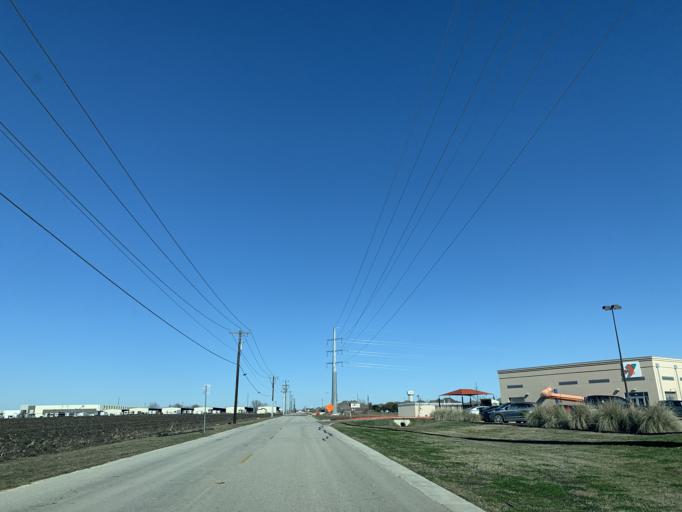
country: US
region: Texas
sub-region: Williamson County
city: Hutto
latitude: 30.5428
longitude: -97.5668
